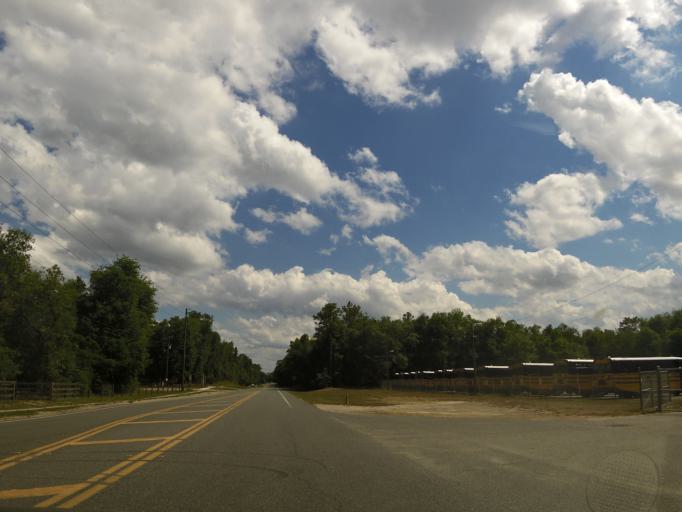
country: US
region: Florida
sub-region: Clay County
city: Keystone Heights
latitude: 29.8161
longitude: -81.9223
